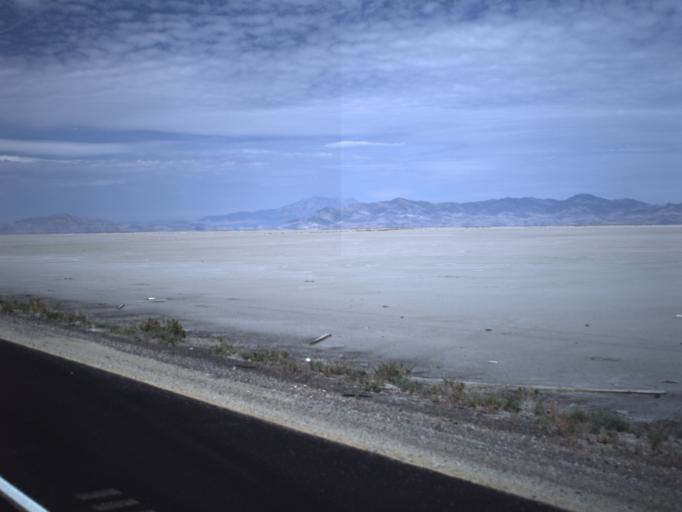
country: US
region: Utah
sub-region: Tooele County
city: Wendover
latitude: 40.7336
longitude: -113.5783
